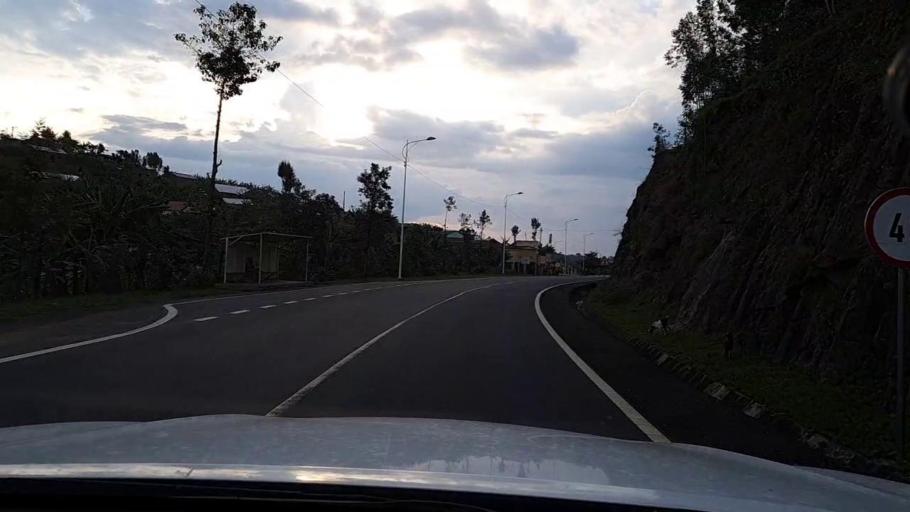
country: RW
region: Western Province
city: Kibuye
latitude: -2.0886
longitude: 29.4035
